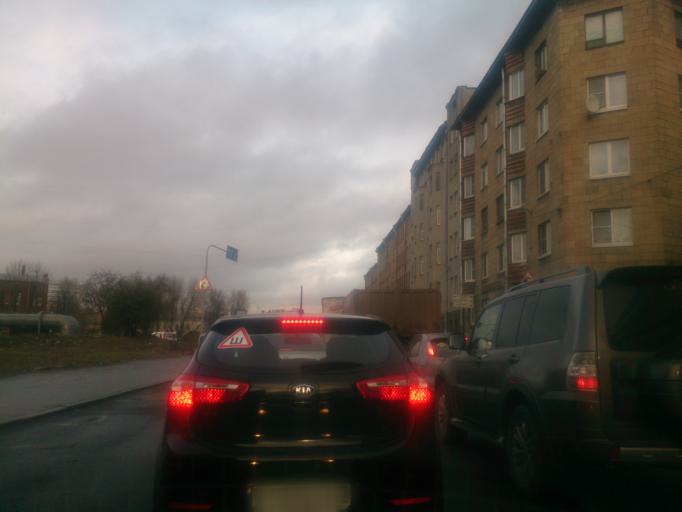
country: RU
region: St.-Petersburg
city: Admiralteisky
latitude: 59.9075
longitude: 30.2947
